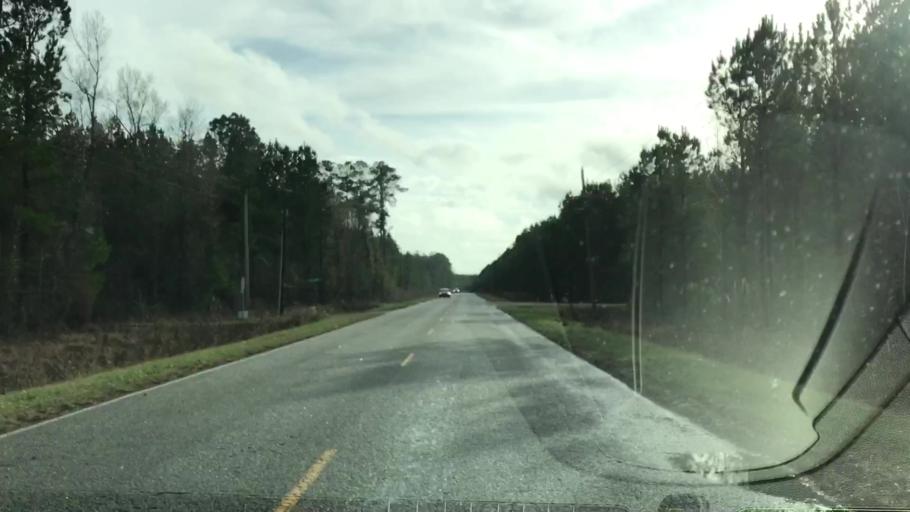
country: US
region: South Carolina
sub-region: Williamsburg County
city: Andrews
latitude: 33.4295
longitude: -79.5941
